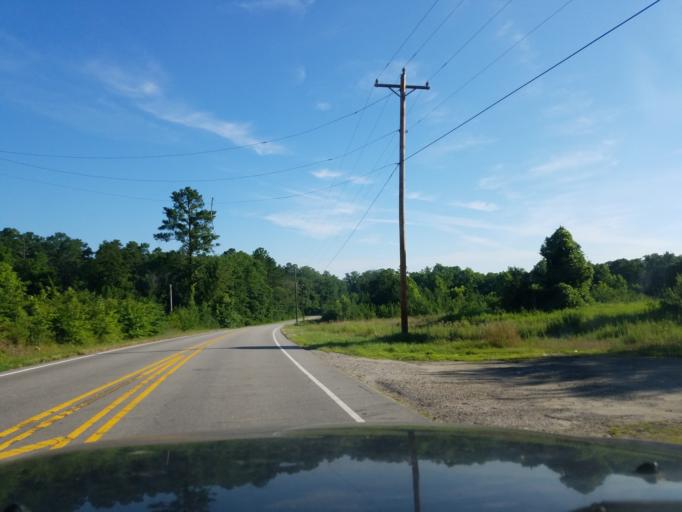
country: US
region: North Carolina
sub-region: Granville County
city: Butner
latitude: 36.1469
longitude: -78.7689
